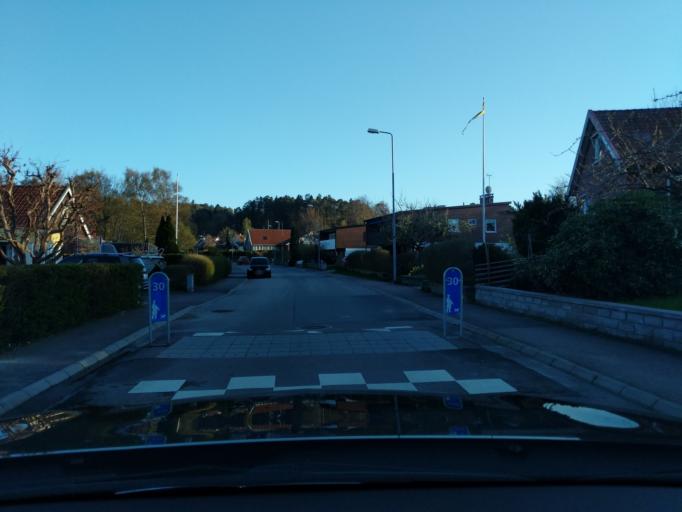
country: SE
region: Vaestra Goetaland
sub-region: Goteborg
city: Majorna
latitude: 57.6367
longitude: 11.9291
